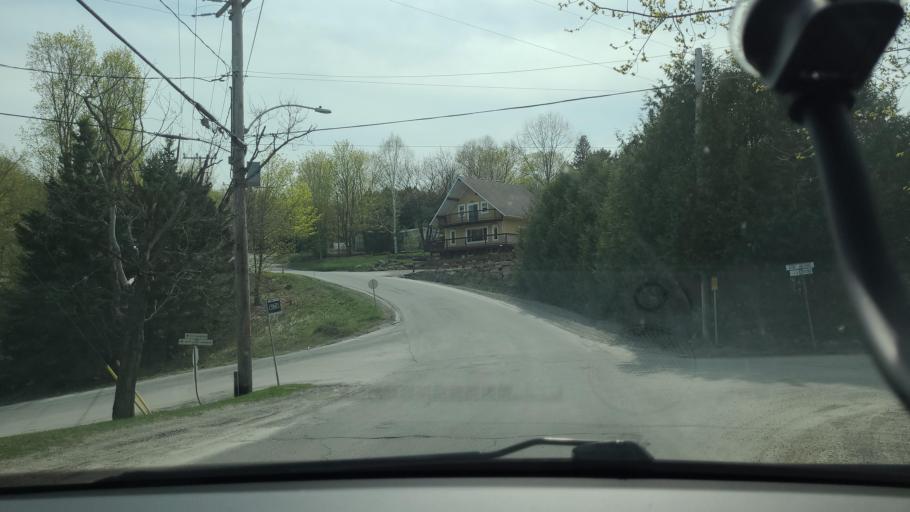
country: CA
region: Quebec
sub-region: Laurentides
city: Prevost
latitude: 45.8939
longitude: -74.0405
